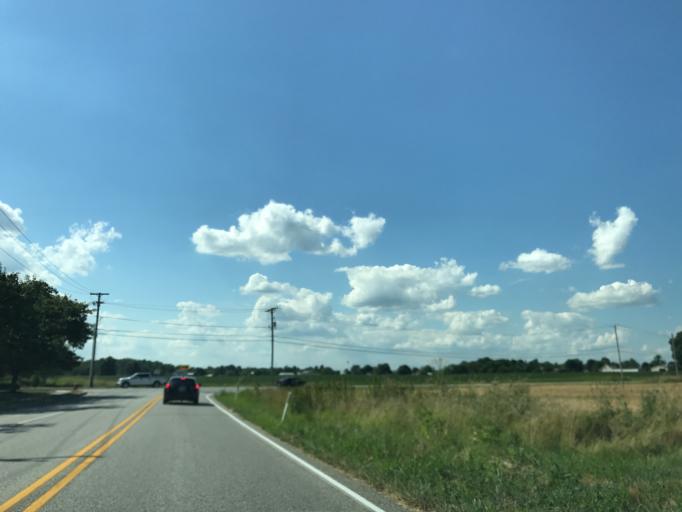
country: US
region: Pennsylvania
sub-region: Adams County
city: McSherrystown
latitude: 39.7911
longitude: -77.0411
